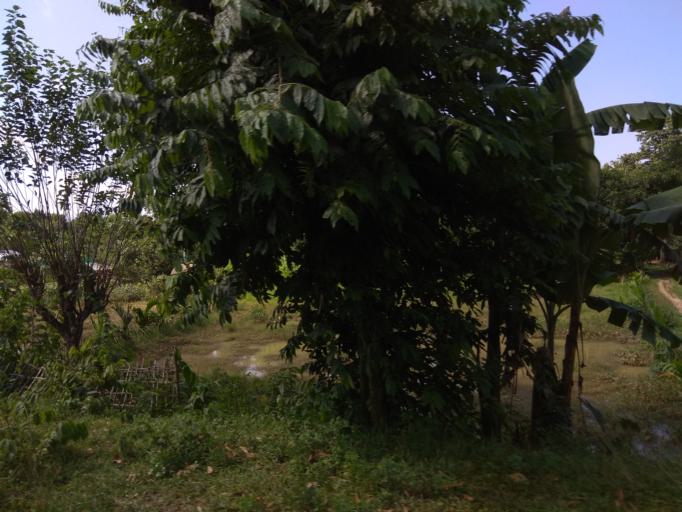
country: BD
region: Chittagong
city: Khagrachhari
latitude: 23.0352
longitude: 92.0069
